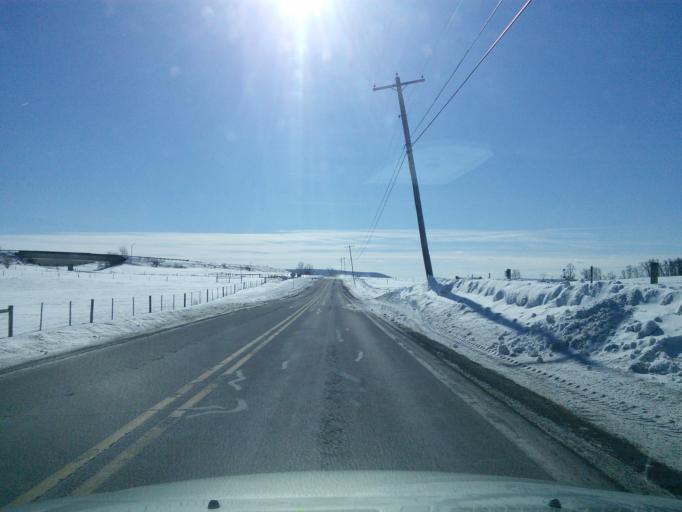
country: US
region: Pennsylvania
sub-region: Centre County
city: Houserville
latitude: 40.8655
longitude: -77.8398
